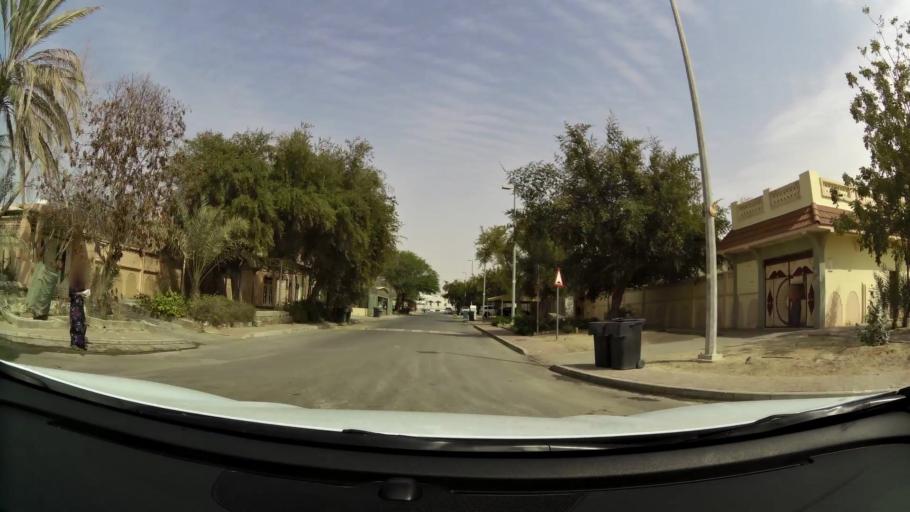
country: AE
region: Abu Dhabi
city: Abu Dhabi
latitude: 24.5472
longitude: 54.6813
